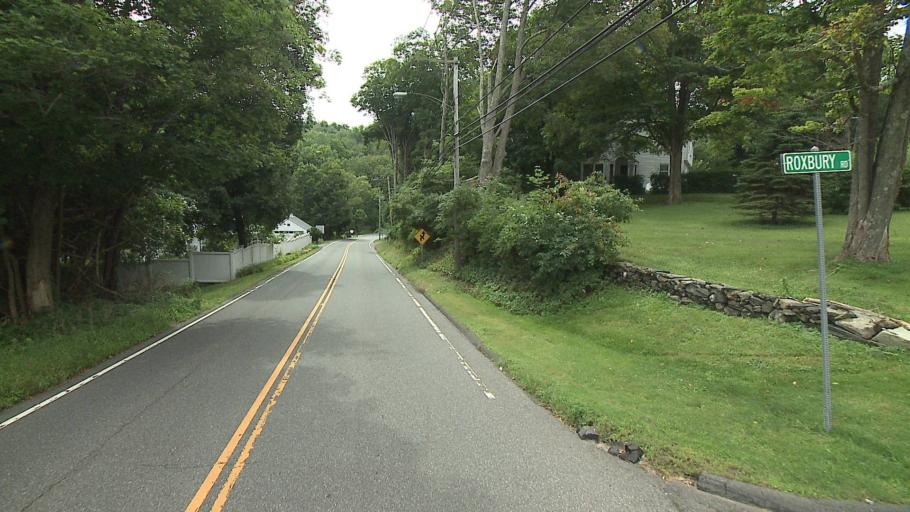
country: US
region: Connecticut
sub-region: Litchfield County
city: New Preston
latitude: 41.6283
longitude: -73.3092
